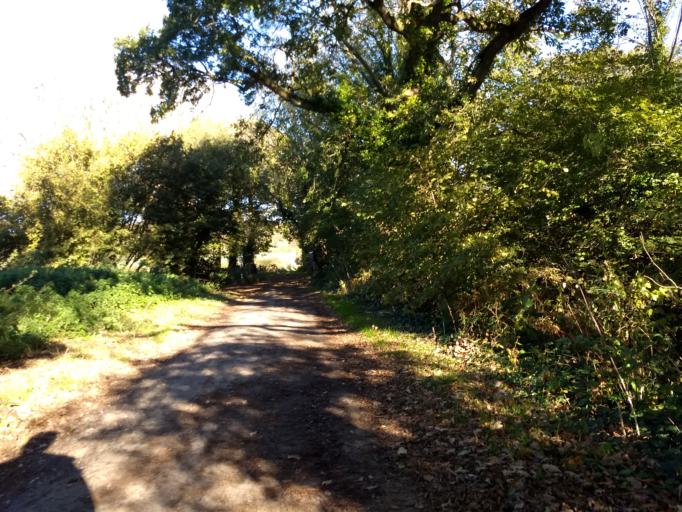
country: GB
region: England
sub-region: Isle of Wight
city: Newport
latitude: 50.6691
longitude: -1.2805
